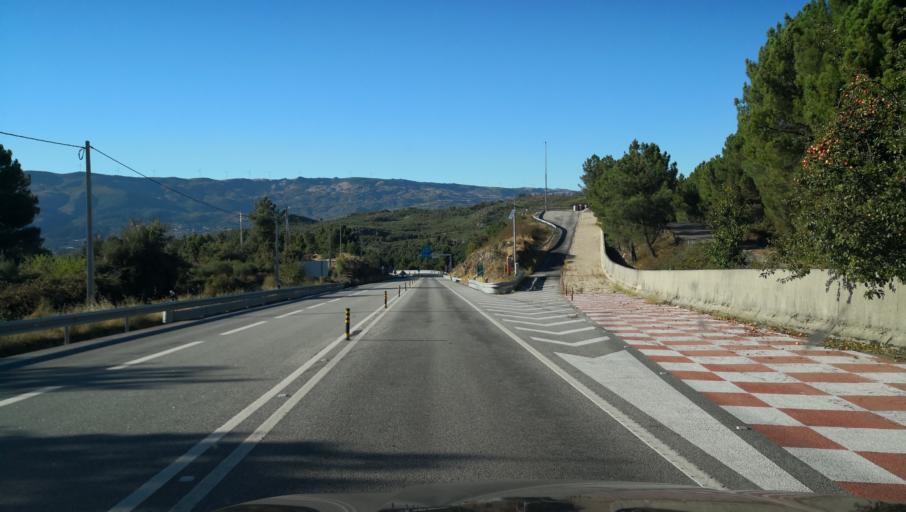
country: PT
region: Vila Real
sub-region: Vila Real
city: Vila Real
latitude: 41.3259
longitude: -7.6704
